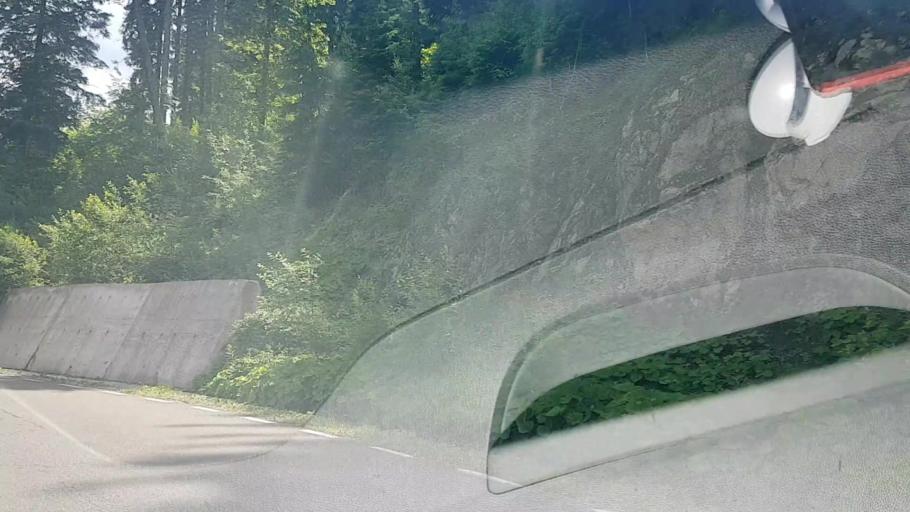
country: RO
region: Suceava
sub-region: Comuna Sadova
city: Sadova
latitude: 47.4623
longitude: 25.5123
